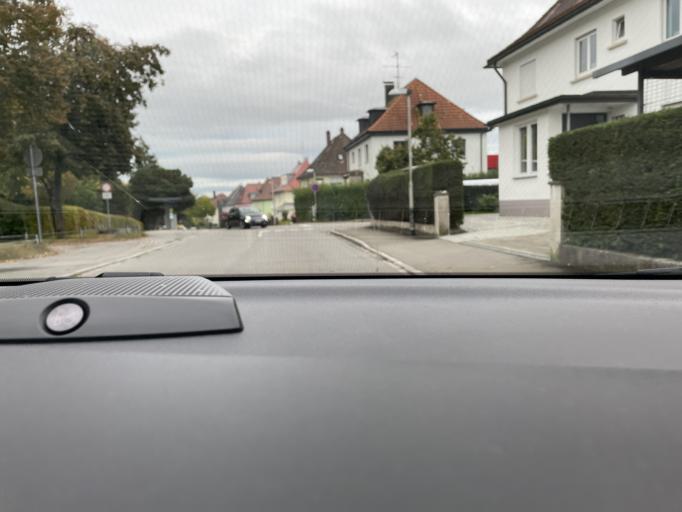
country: DE
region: Baden-Wuerttemberg
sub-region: Tuebingen Region
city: Friedrichshafen
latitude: 47.6582
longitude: 9.4593
